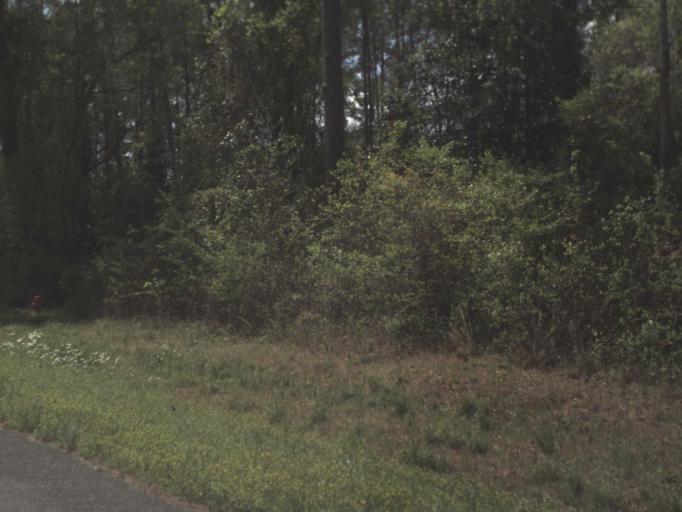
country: US
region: Florida
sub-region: Okaloosa County
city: Crestview
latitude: 30.9721
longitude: -86.6312
